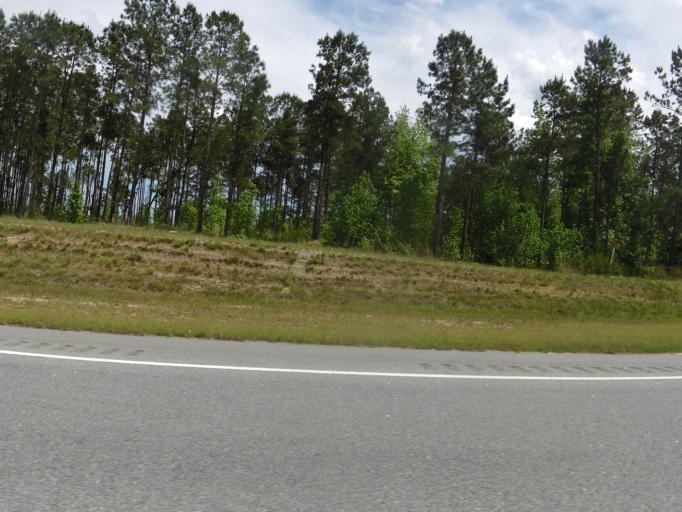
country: US
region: Georgia
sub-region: Jefferson County
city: Wadley
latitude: 32.7545
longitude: -82.3888
